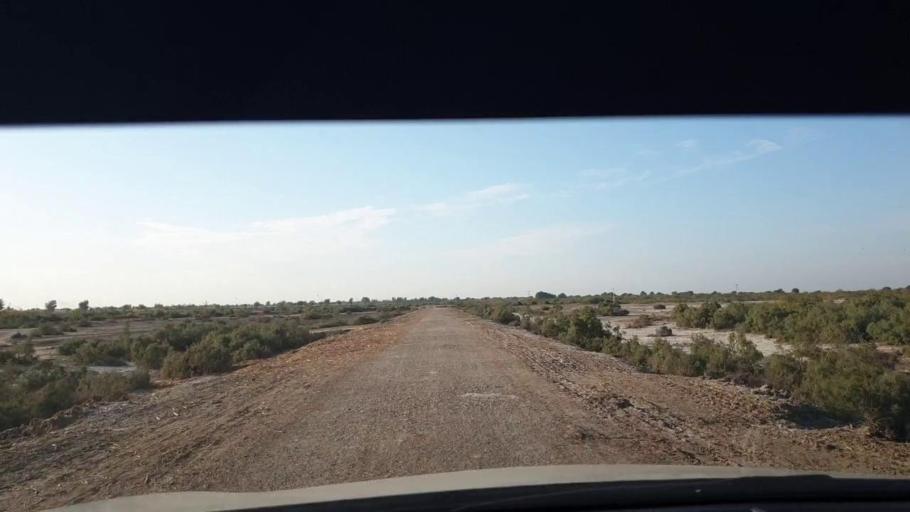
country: PK
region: Sindh
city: Berani
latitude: 25.8227
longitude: 68.9063
